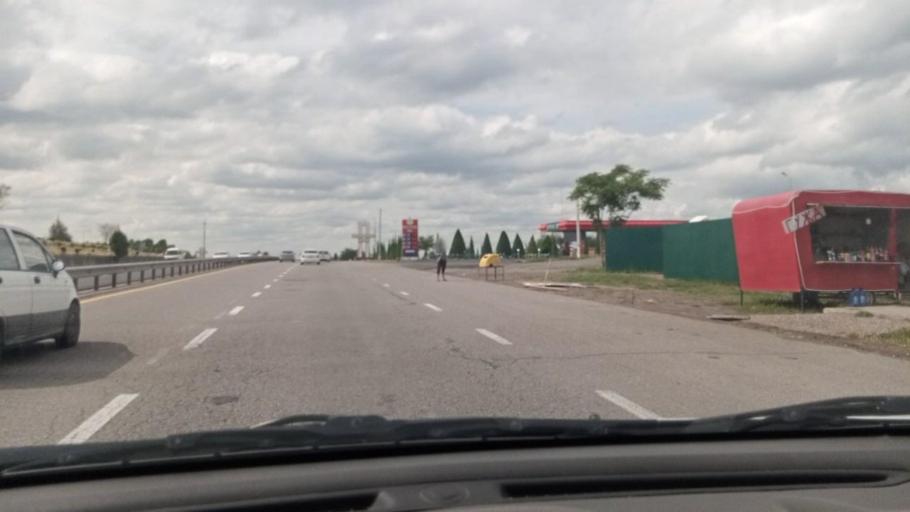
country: UZ
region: Toshkent
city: Tuytepa
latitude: 41.1214
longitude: 69.4413
